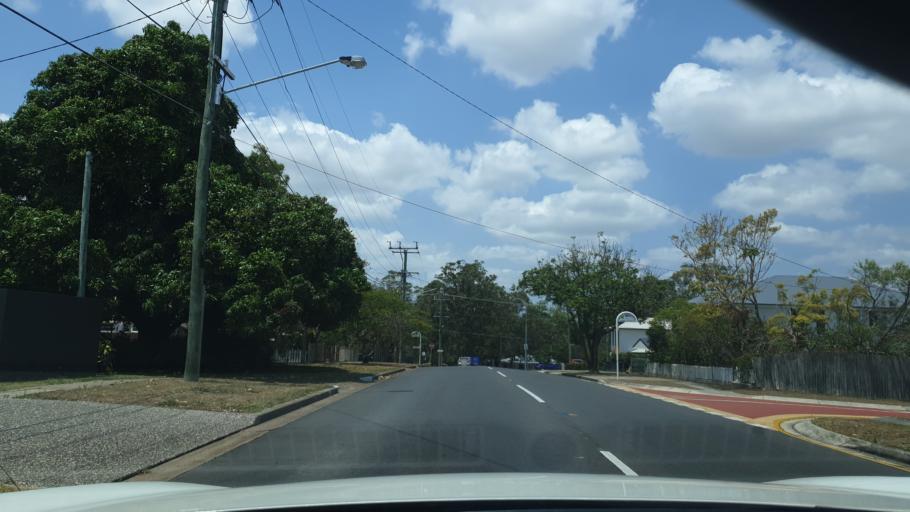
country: AU
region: Queensland
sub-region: Brisbane
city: Chermside West
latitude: -27.3717
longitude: 153.0252
